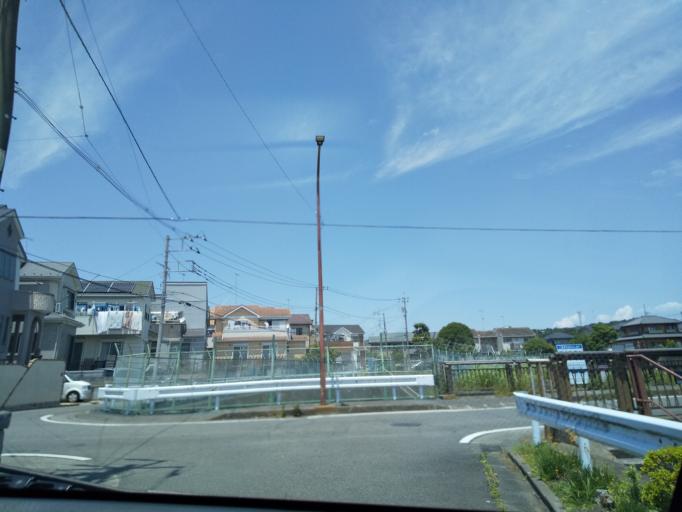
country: JP
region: Kanagawa
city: Zama
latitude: 35.5301
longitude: 139.3782
